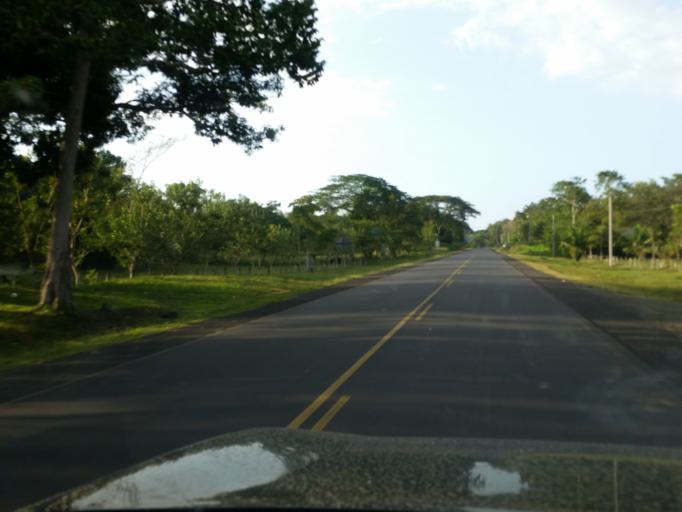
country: NI
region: Rio San Juan
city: San Miguelito
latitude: 11.3579
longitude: -84.7629
